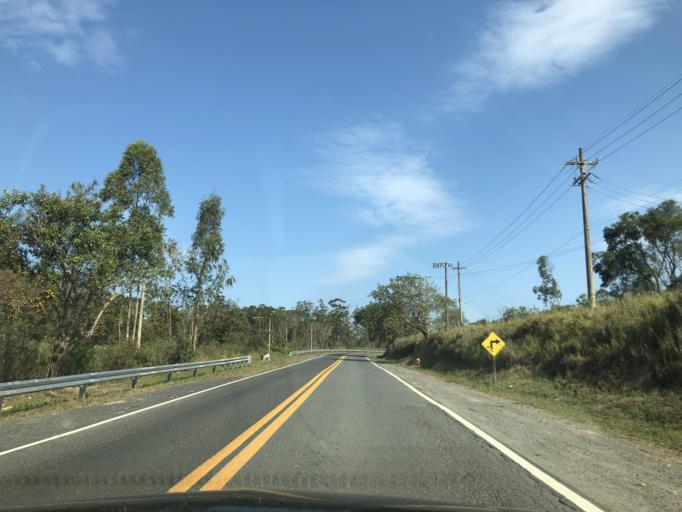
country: BR
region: Sao Paulo
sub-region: Pilar Do Sul
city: Pilar do Sul
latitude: -23.8235
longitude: -47.6638
